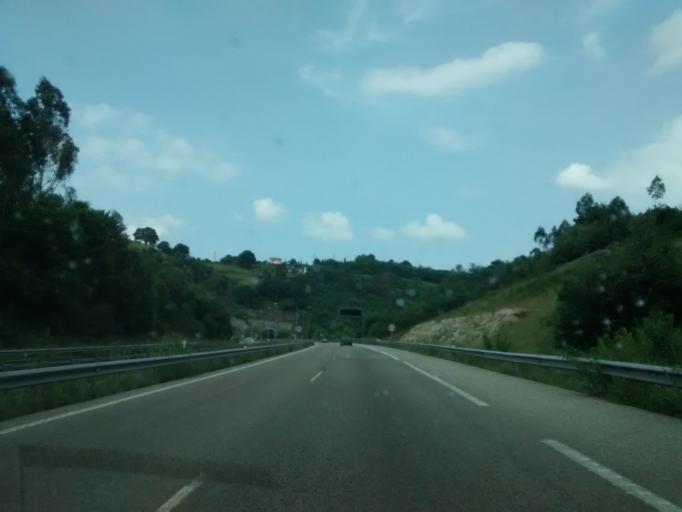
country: ES
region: Asturias
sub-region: Province of Asturias
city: Mieres
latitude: 43.2824
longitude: -5.7606
